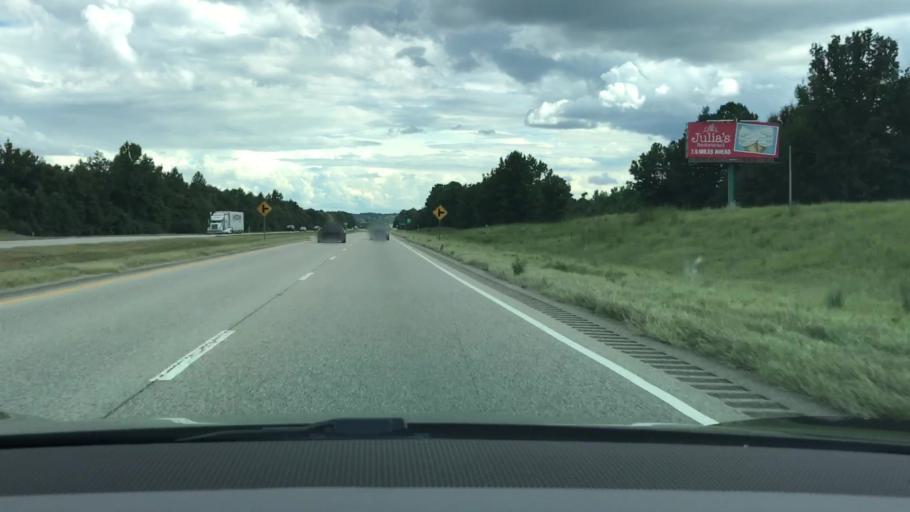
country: US
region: Alabama
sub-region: Pike County
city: Troy
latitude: 31.8663
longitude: -85.9999
